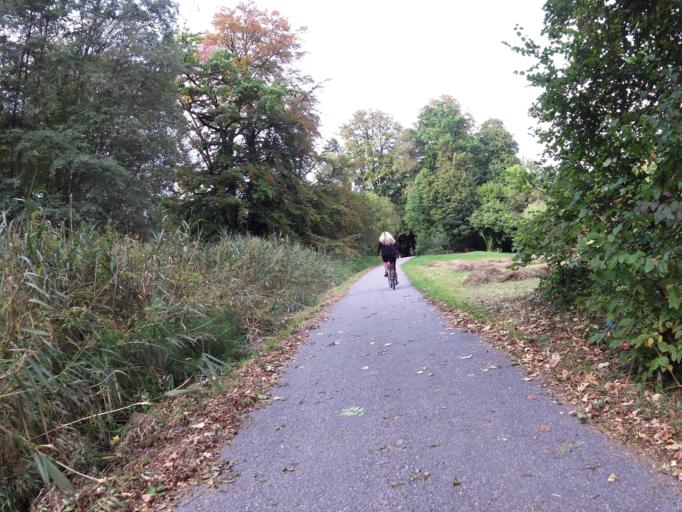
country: DE
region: Bavaria
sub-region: Upper Bavaria
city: Bernried
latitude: 47.8648
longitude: 11.2976
